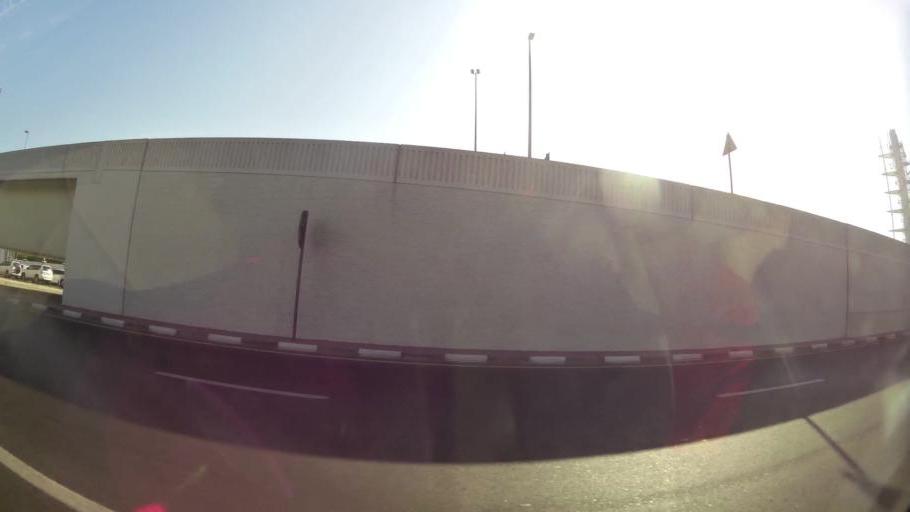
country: AE
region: Ash Shariqah
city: Sharjah
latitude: 25.2735
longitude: 55.3501
